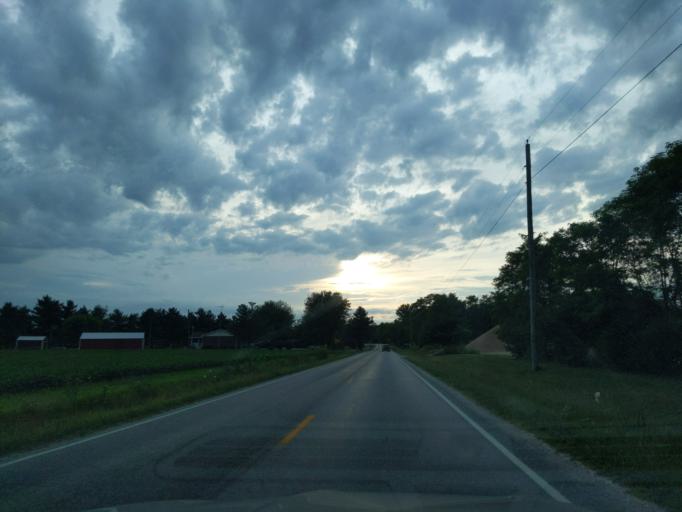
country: US
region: Indiana
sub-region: Ripley County
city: Osgood
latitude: 39.2035
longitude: -85.3172
